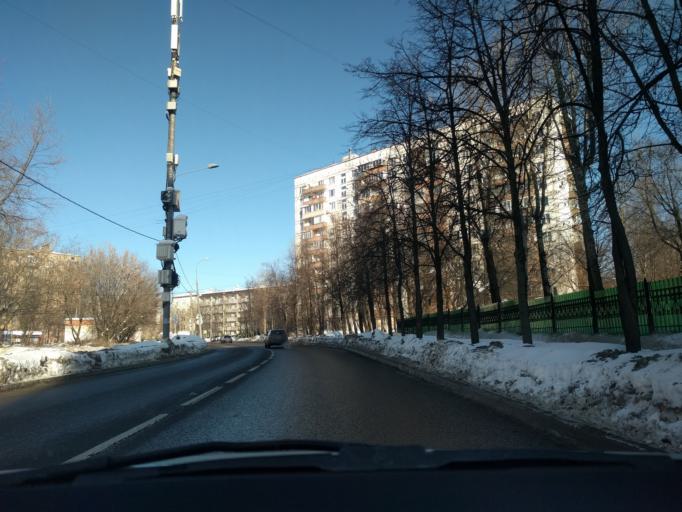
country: RU
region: Moscow
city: Gol'yanovo
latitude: 55.8002
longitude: 37.8271
